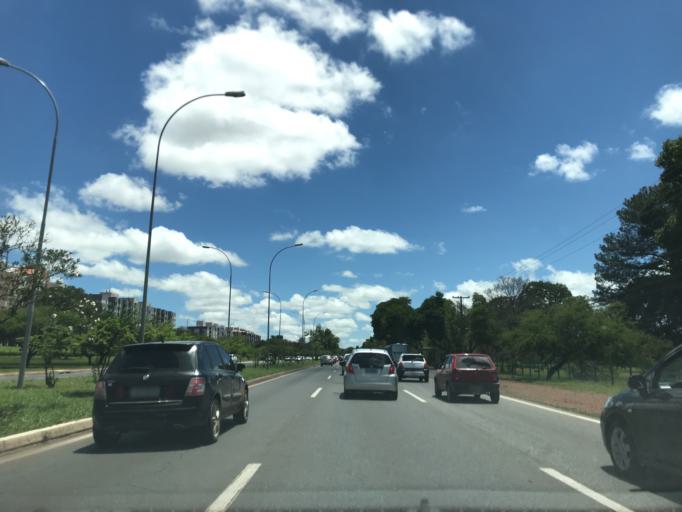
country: BR
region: Federal District
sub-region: Brasilia
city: Brasilia
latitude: -15.8024
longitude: -47.9200
